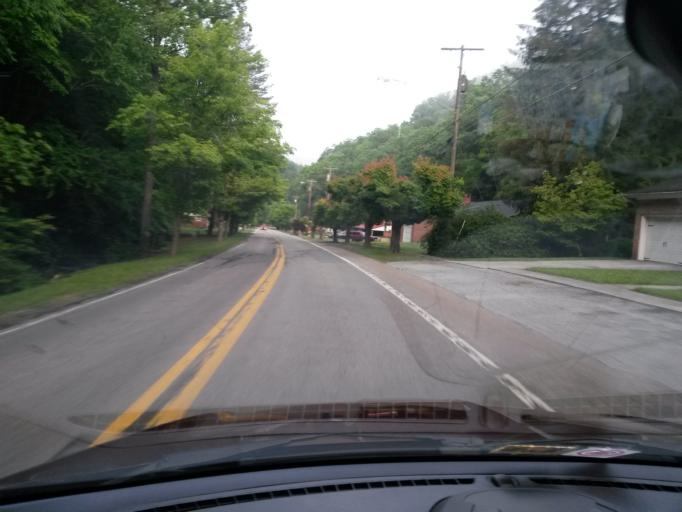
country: US
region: West Virginia
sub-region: McDowell County
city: Welch
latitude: 37.4481
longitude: -81.5571
